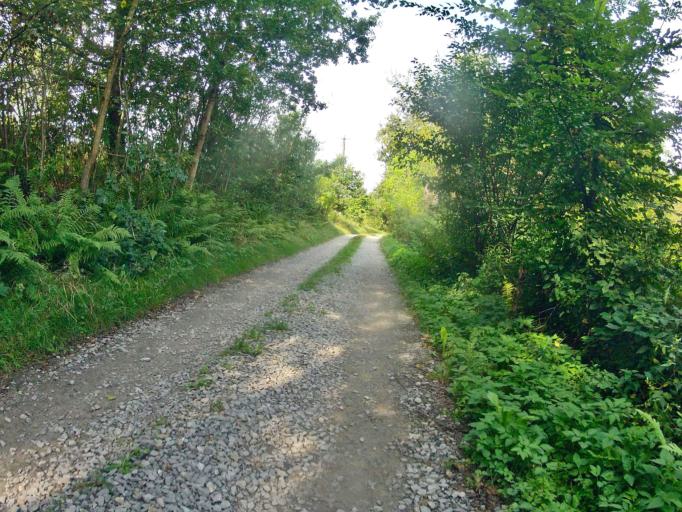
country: PL
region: Subcarpathian Voivodeship
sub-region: Powiat jasielski
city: Brzyska
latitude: 49.7961
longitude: 21.3698
